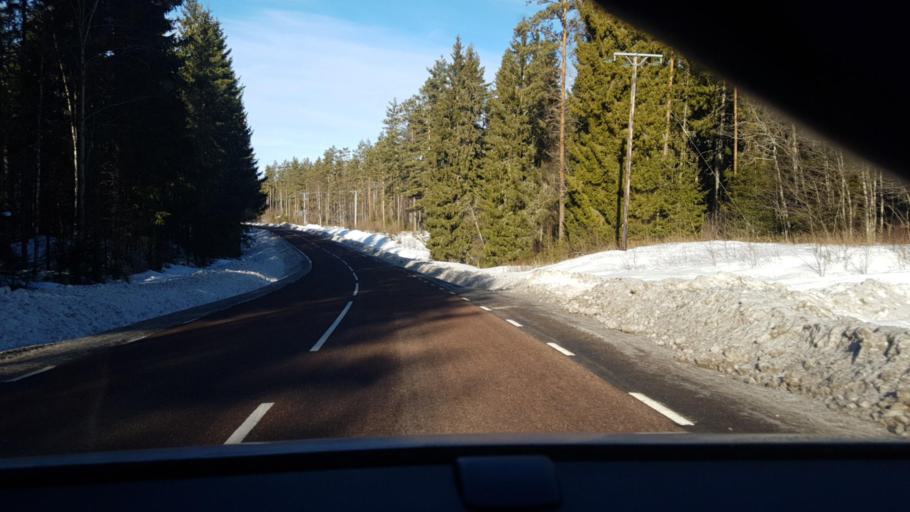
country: SE
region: Vaermland
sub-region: Eda Kommun
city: Charlottenberg
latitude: 59.8087
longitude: 12.2036
